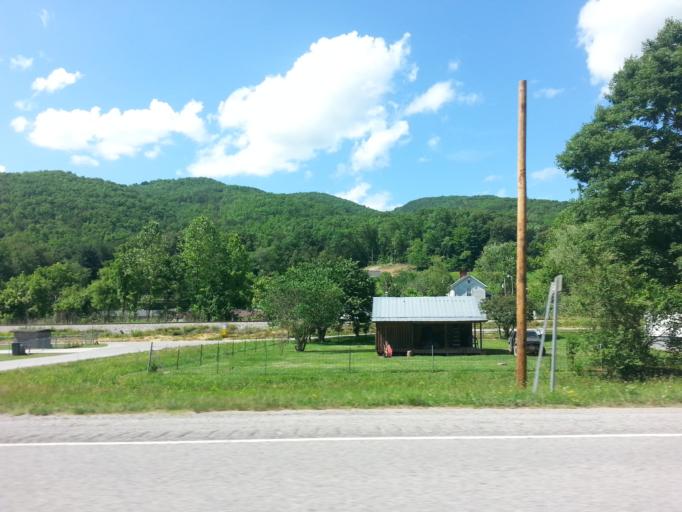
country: US
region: Kentucky
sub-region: Harlan County
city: Harlan
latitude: 36.9250
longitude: -83.1656
